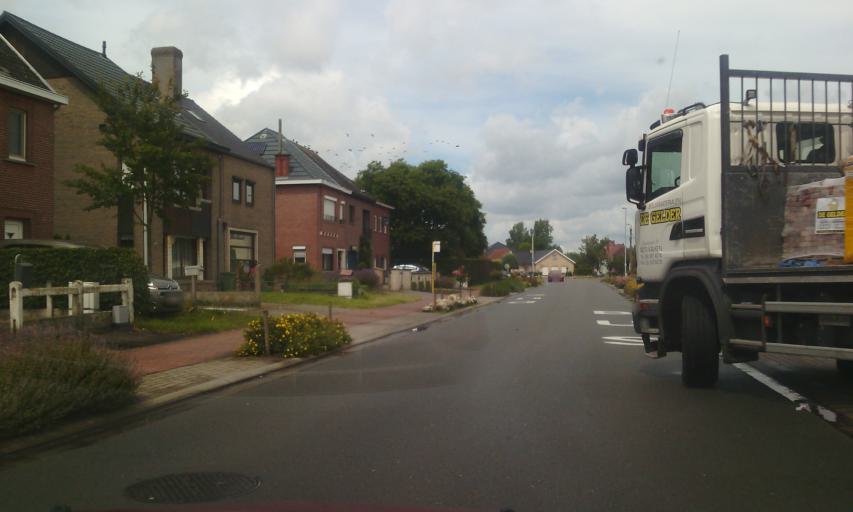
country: BE
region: Flanders
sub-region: Provincie Oost-Vlaanderen
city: Wetteren
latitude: 51.0179
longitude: 3.8705
